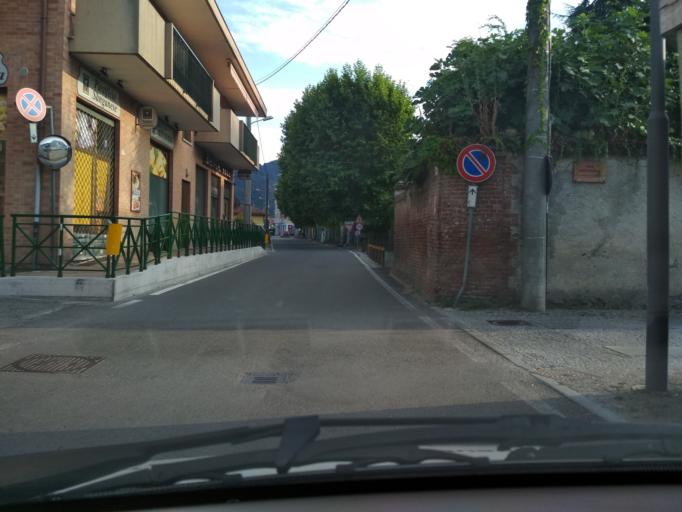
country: IT
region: Piedmont
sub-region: Provincia di Torino
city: Sangano
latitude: 45.0286
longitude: 7.4514
